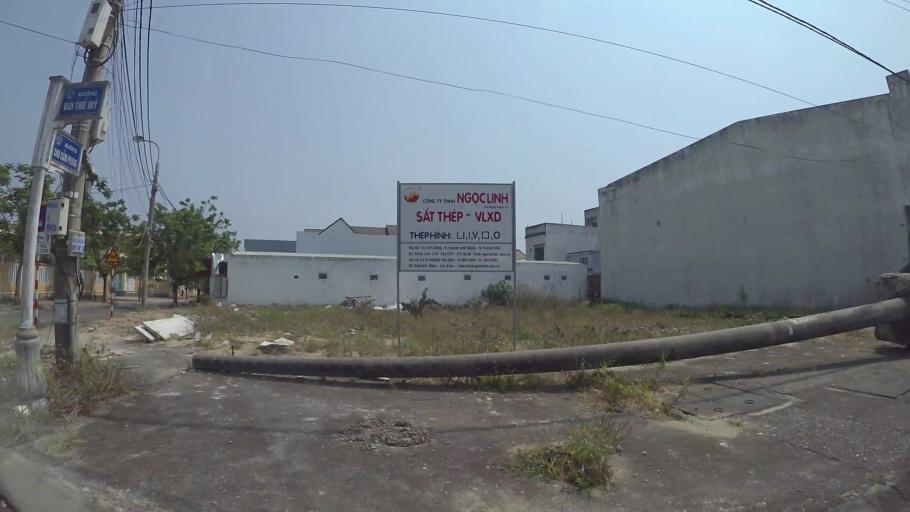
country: VN
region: Da Nang
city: Ngu Hanh Son
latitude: 16.0134
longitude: 108.2515
